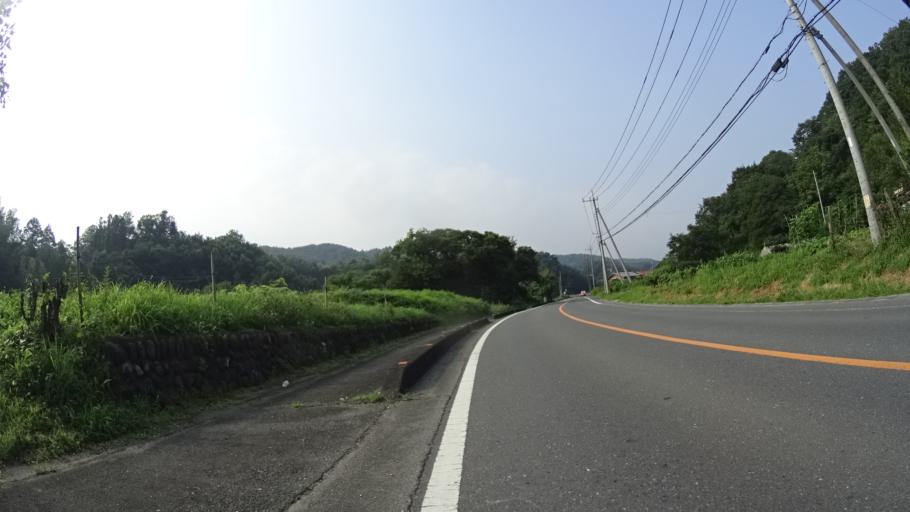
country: JP
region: Saitama
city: Chichibu
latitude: 36.0110
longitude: 139.0537
